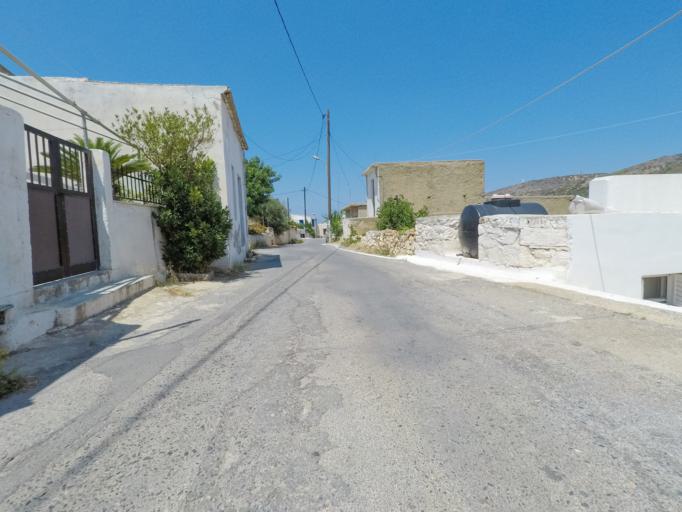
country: GR
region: Crete
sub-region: Nomos Lasithiou
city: Elounda
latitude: 35.3160
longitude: 25.7340
